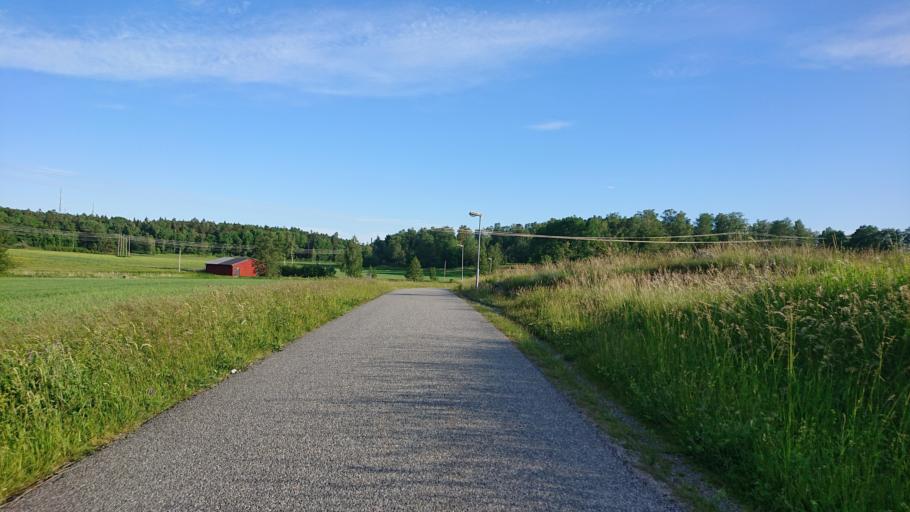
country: SE
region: Stockholm
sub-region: Osterakers Kommun
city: Akersberga
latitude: 59.4985
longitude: 18.3022
